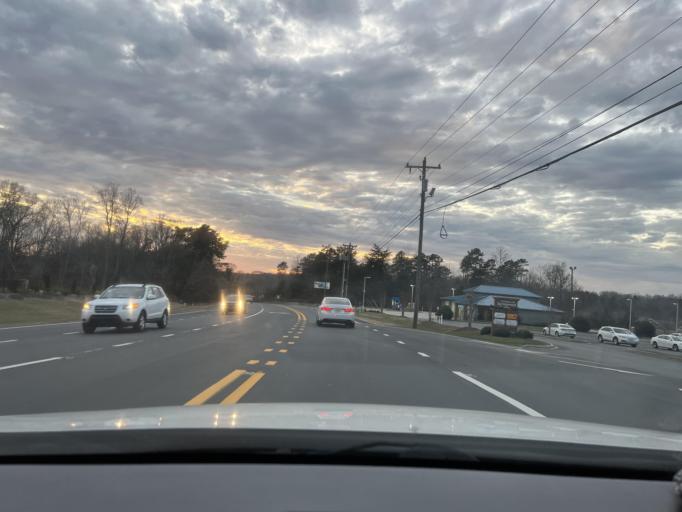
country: US
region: North Carolina
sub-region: Guilford County
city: Gibsonville
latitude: 36.0811
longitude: -79.5395
